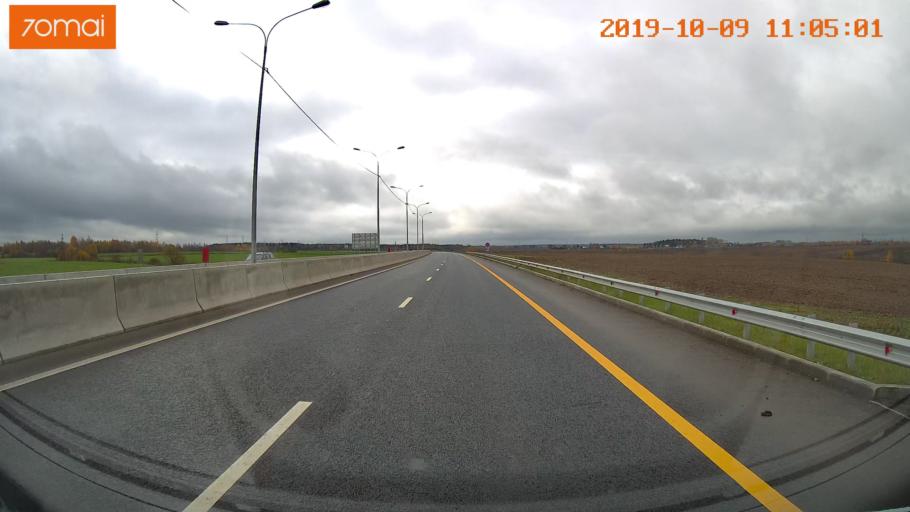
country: RU
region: Vologda
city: Molochnoye
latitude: 59.2052
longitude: 39.7609
